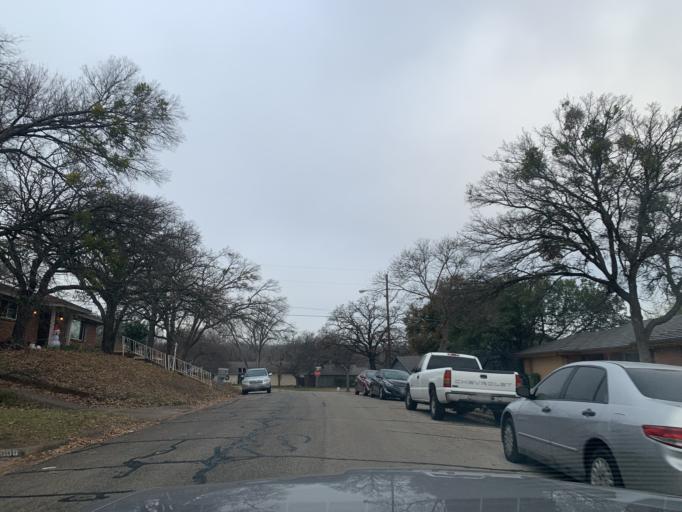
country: US
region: Texas
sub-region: Tarrant County
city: Bedford
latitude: 32.8311
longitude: -97.1535
